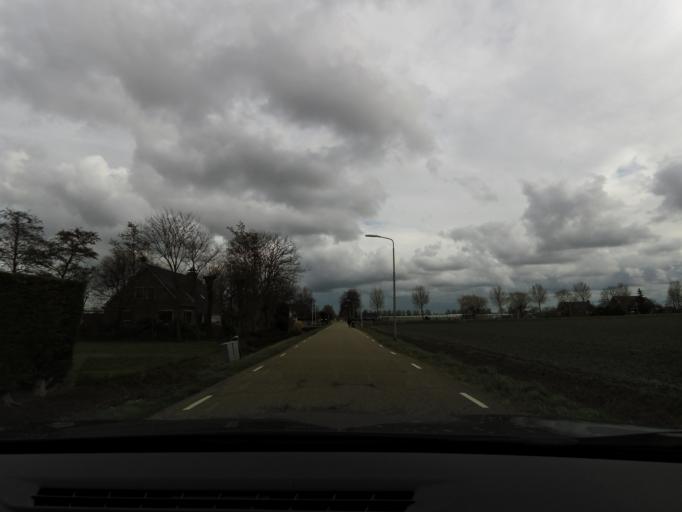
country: NL
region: North Holland
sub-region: Gemeente Uithoorn
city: Uithoorn
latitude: 52.2746
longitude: 4.8175
